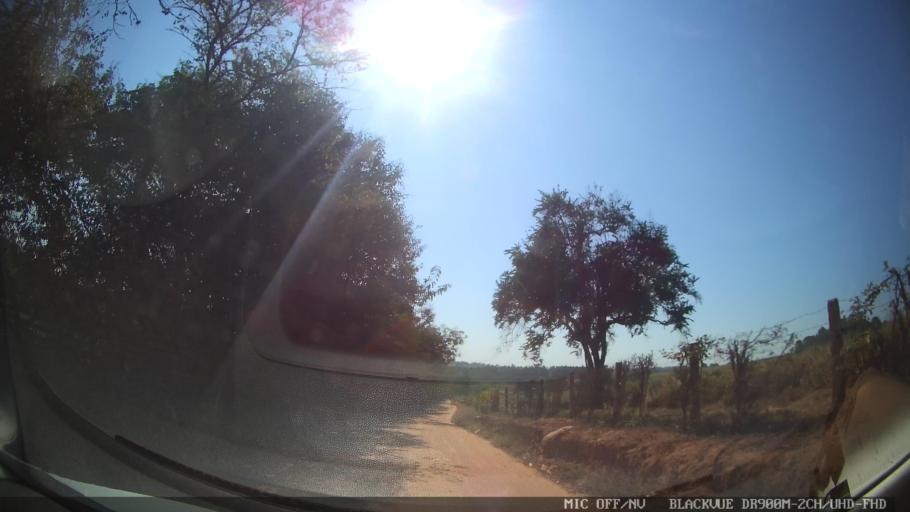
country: BR
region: Sao Paulo
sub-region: Itupeva
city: Itupeva
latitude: -23.0676
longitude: -47.0940
